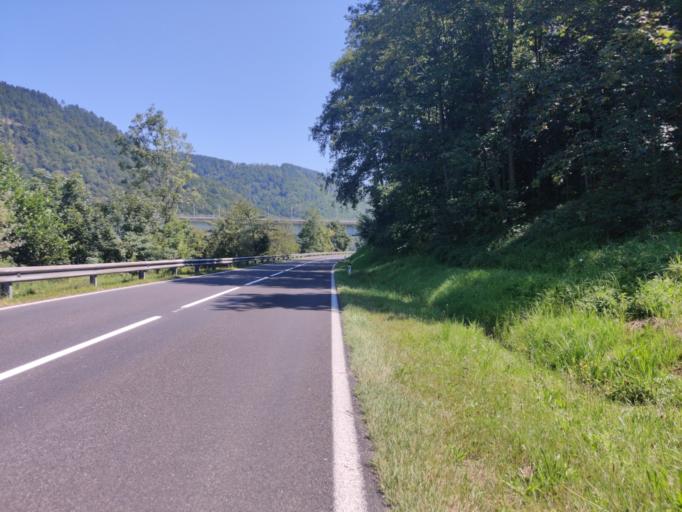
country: AT
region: Upper Austria
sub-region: Politischer Bezirk Rohrbach
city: Pfarrkirchen im Muehlkreis
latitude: 48.4650
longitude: 13.7933
